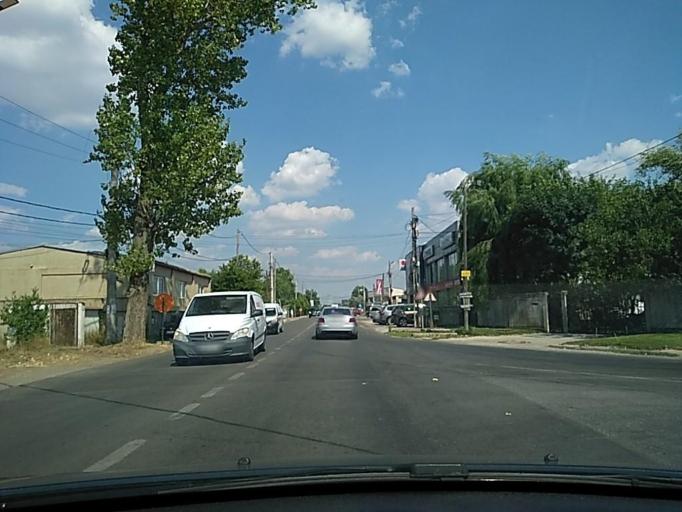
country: RO
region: Ilfov
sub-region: Comuna Clinceni
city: Olteni
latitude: 44.4035
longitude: 25.9581
